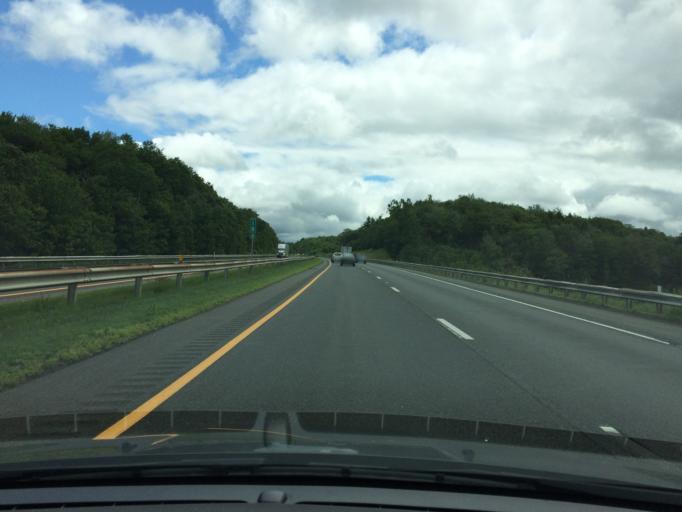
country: US
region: Massachusetts
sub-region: Berkshire County
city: Otis
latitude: 42.2479
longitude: -73.1102
